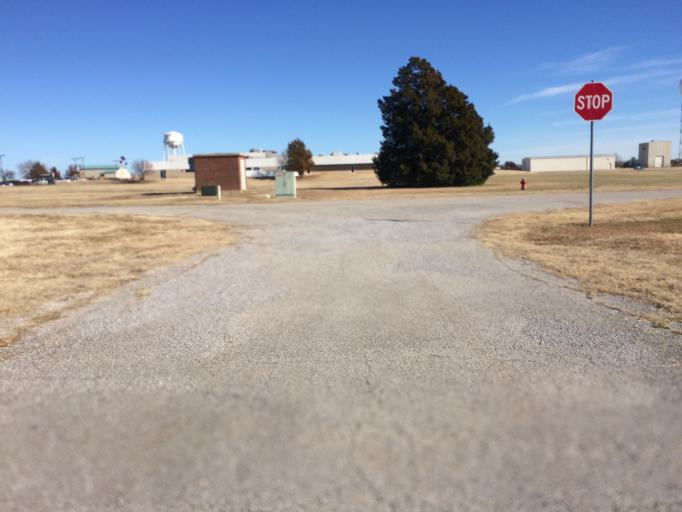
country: US
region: Oklahoma
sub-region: Cleveland County
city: Norman
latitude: 35.2396
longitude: -97.4634
